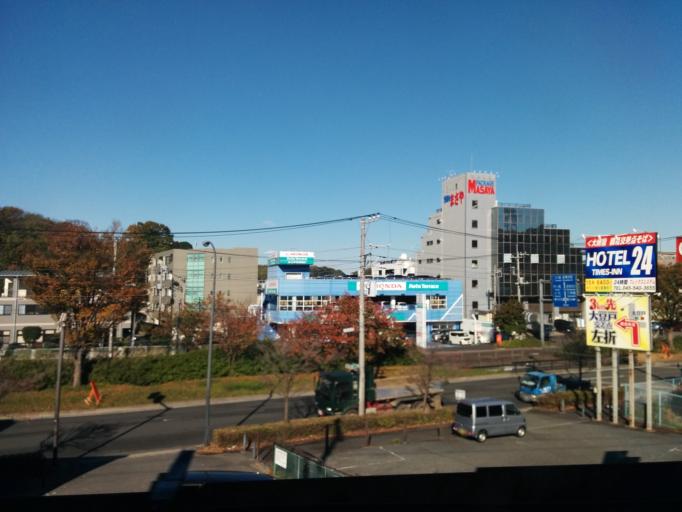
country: JP
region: Kanagawa
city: Yokohama
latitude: 35.4988
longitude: 139.6070
